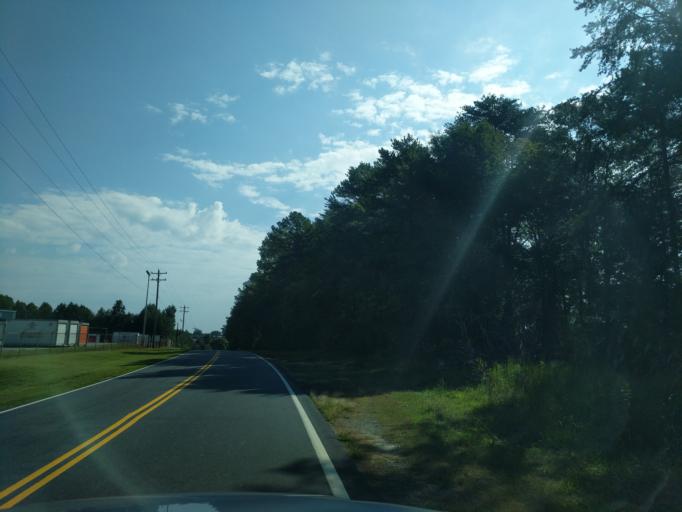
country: US
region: South Carolina
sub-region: Spartanburg County
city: Wellford
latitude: 34.9395
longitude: -82.0866
